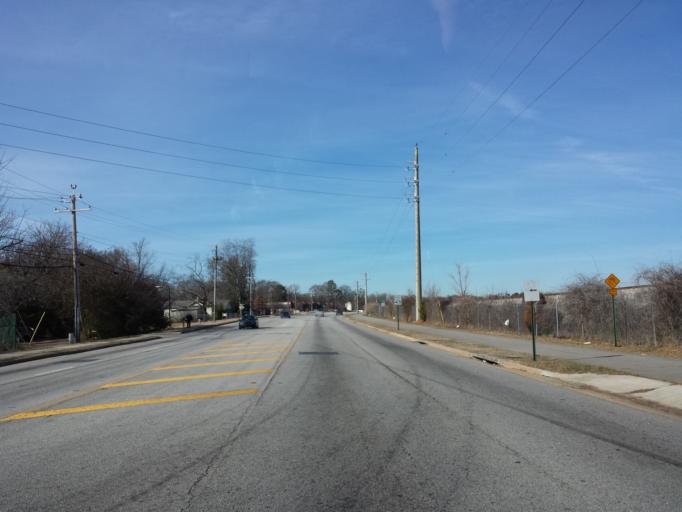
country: US
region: Georgia
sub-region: Cobb County
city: Fair Oaks
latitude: 33.9165
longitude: -84.5395
